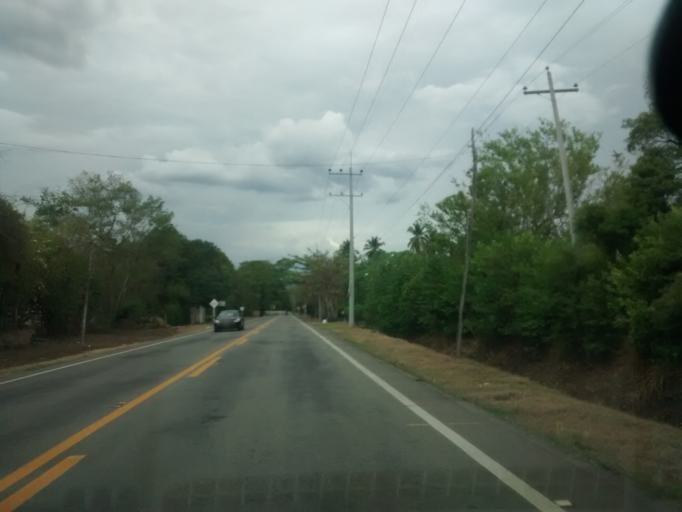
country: CO
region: Cundinamarca
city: Tocaima
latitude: 4.4434
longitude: -74.6719
